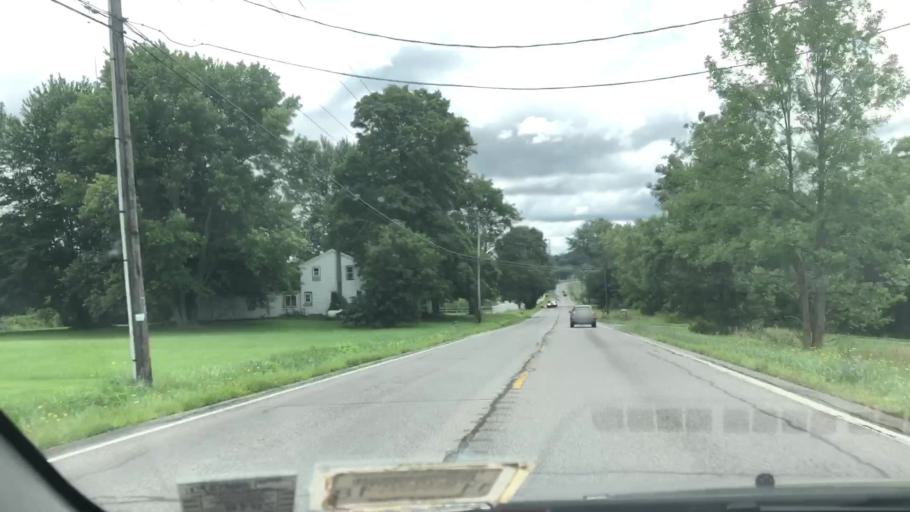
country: US
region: New York
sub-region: Wayne County
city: Macedon
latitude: 43.1055
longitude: -77.2930
